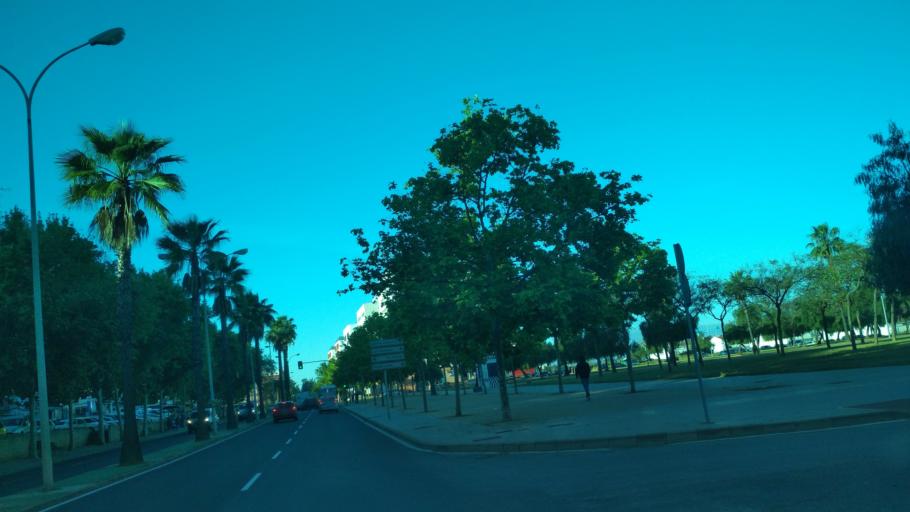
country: ES
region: Andalusia
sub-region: Provincia de Huelva
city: Huelva
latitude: 37.2771
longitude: -6.9488
